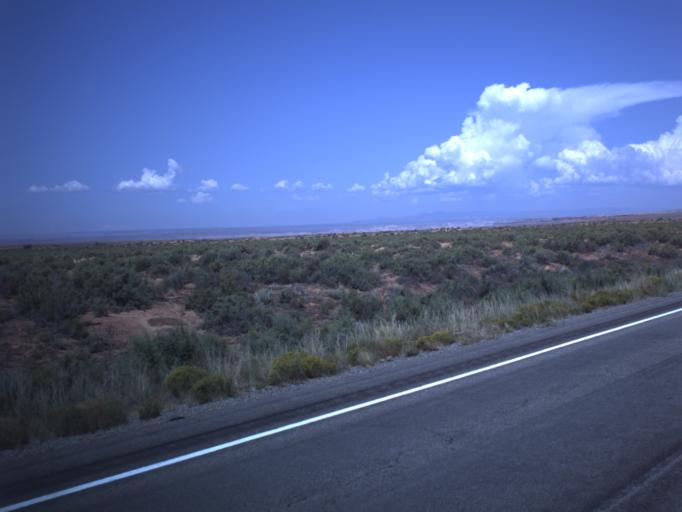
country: US
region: Utah
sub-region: San Juan County
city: Blanding
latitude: 37.1047
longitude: -109.5467
